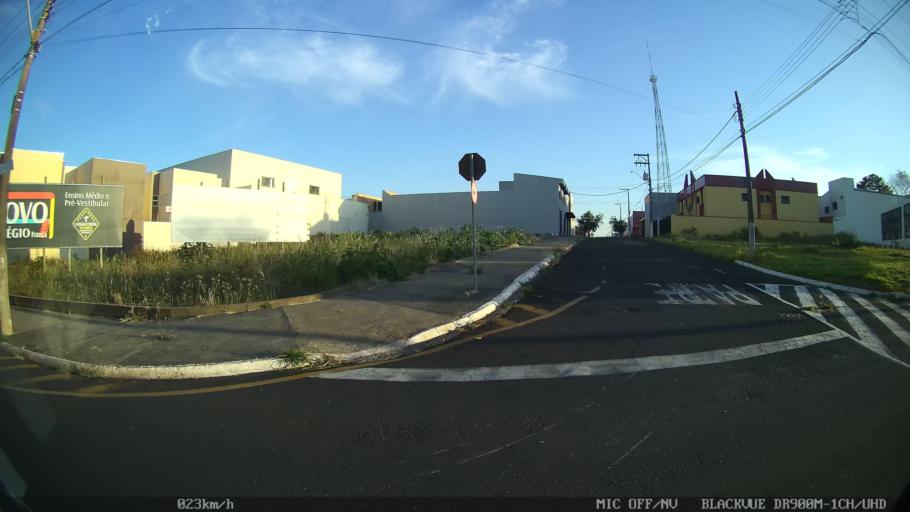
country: BR
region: Sao Paulo
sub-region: Franca
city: Franca
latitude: -20.5121
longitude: -47.3855
